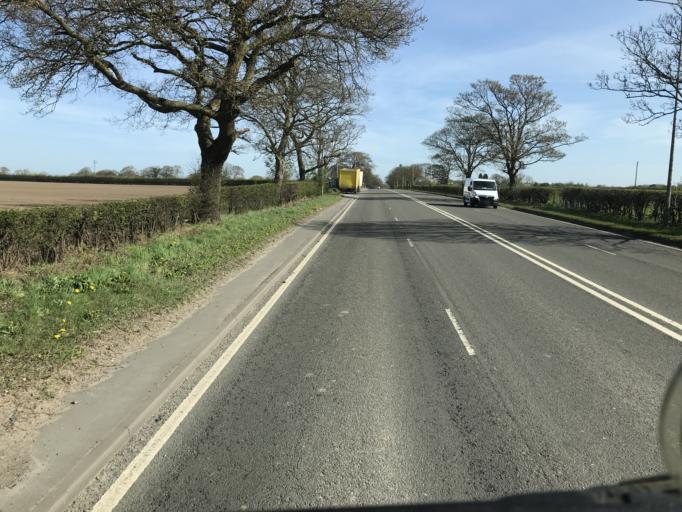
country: GB
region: England
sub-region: Cheshire East
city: Mere
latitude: 53.2836
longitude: -2.4336
